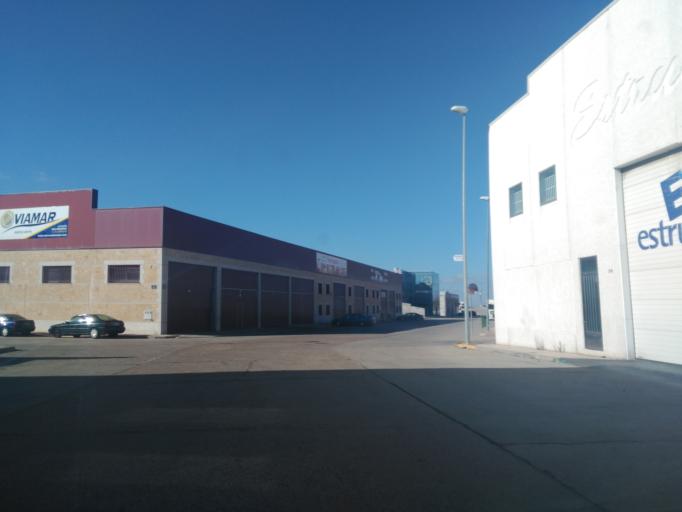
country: ES
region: Castille and Leon
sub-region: Provincia de Salamanca
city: Villares de la Reina
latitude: 40.9931
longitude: -5.6429
